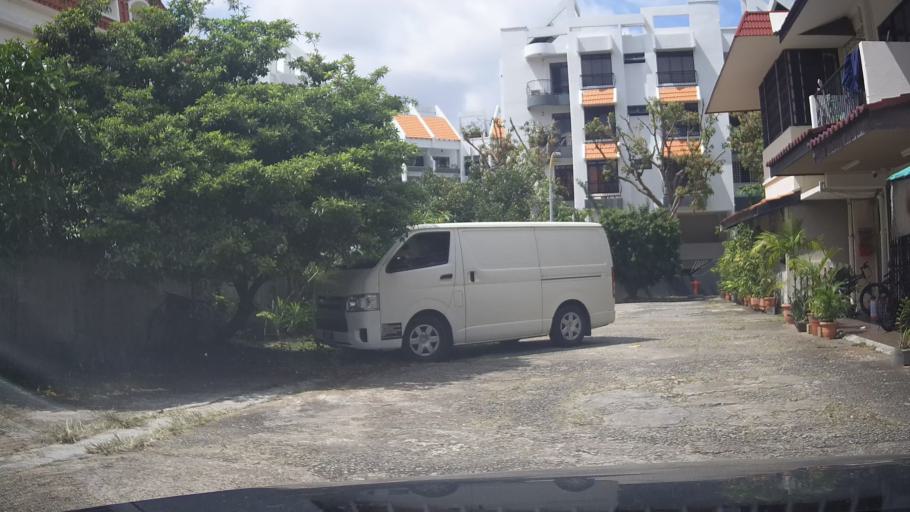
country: SG
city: Singapore
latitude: 1.3067
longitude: 103.9004
